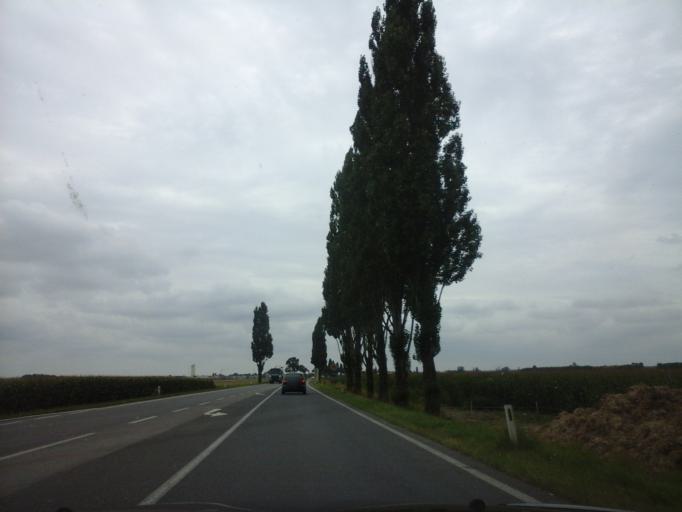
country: AT
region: Lower Austria
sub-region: Politischer Bezirk Ganserndorf
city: Engelhartstetten
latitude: 48.1626
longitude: 16.8969
